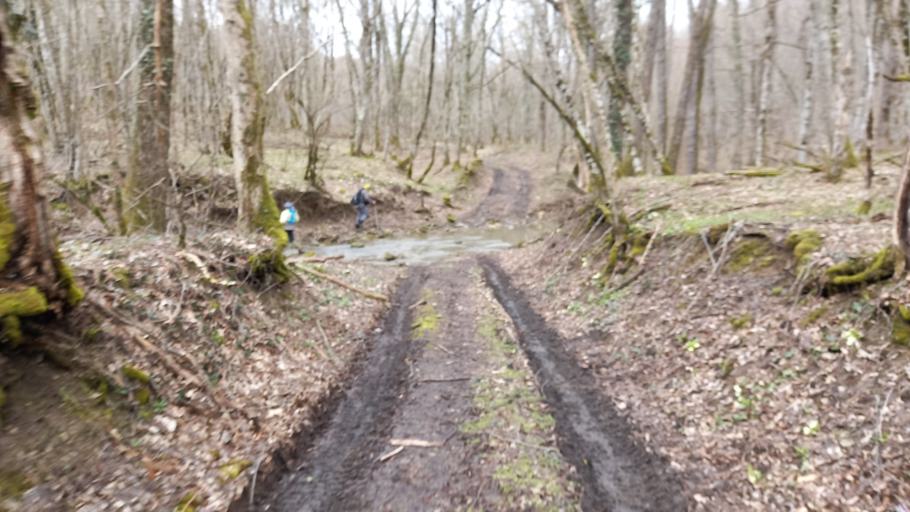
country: RU
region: Krasnodarskiy
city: Pshada
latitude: 44.4911
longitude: 38.3913
